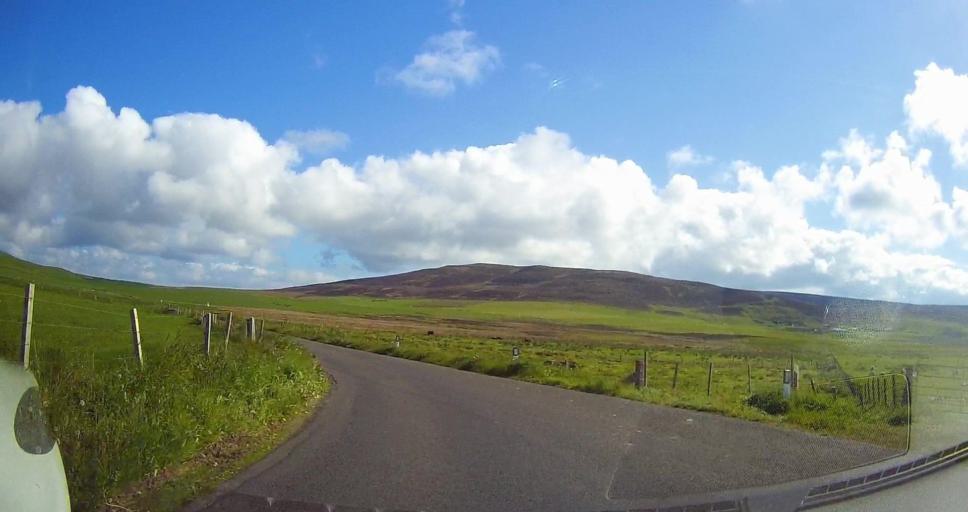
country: GB
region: Scotland
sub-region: Orkney Islands
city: Stromness
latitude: 58.9853
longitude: -3.1479
